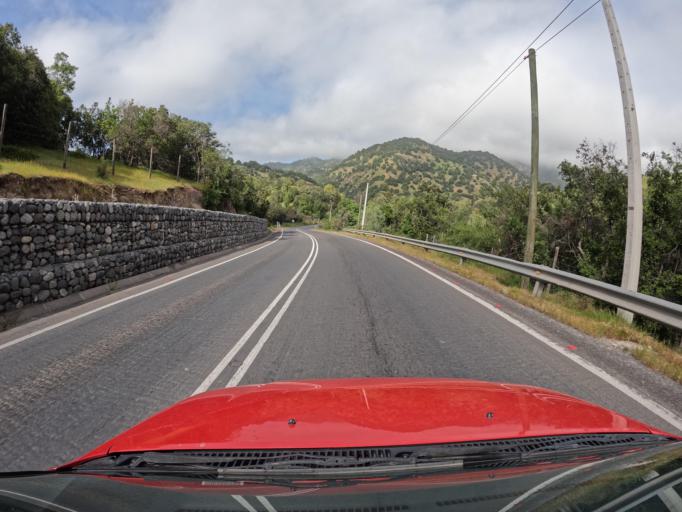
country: CL
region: Maule
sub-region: Provincia de Curico
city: Teno
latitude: -34.8165
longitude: -71.2051
